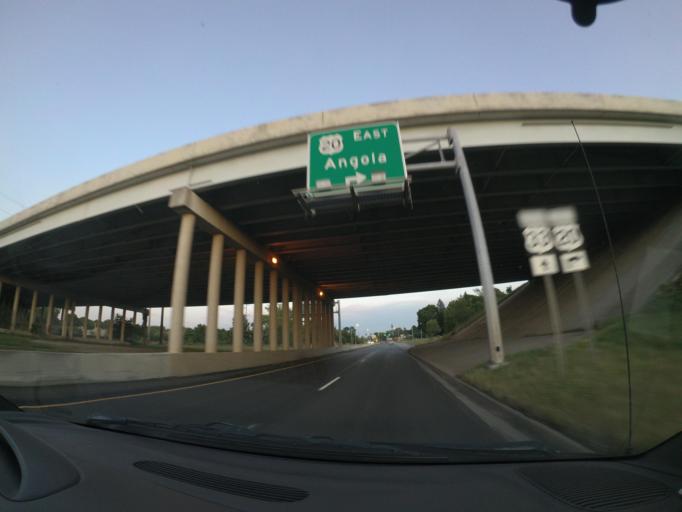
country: US
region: Indiana
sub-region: Elkhart County
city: Dunlap
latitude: 41.6522
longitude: -85.9414
